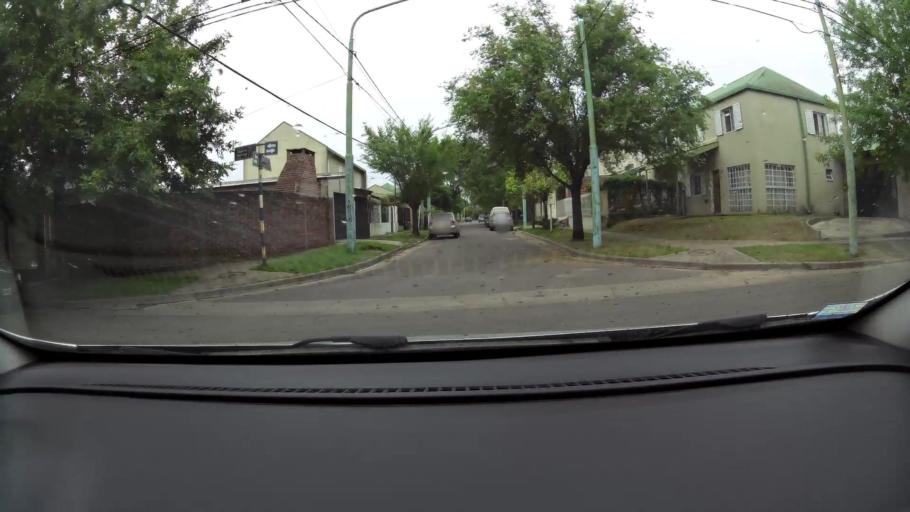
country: AR
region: Buenos Aires
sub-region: Partido de Campana
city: Campana
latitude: -34.2008
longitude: -58.9418
